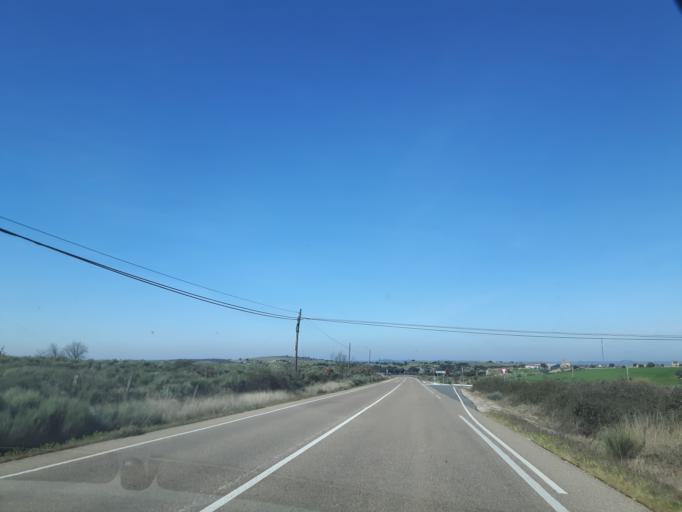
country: ES
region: Castille and Leon
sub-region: Provincia de Salamanca
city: Guadramiro
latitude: 41.0122
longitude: -6.4792
